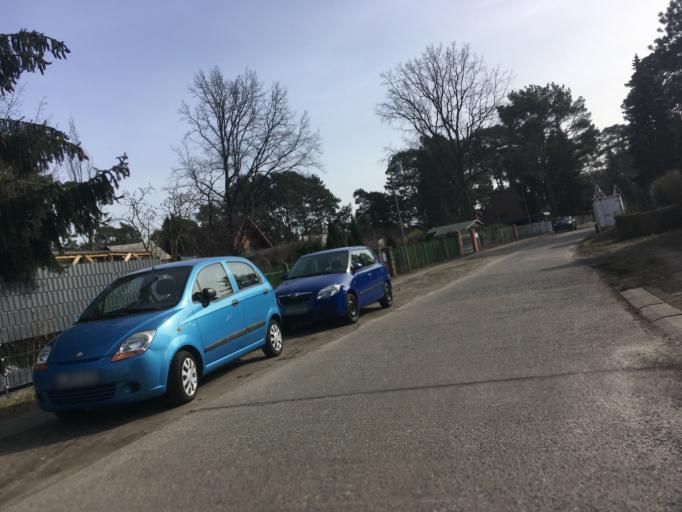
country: DE
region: Berlin
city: Schmockwitz
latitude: 52.3929
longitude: 13.6293
